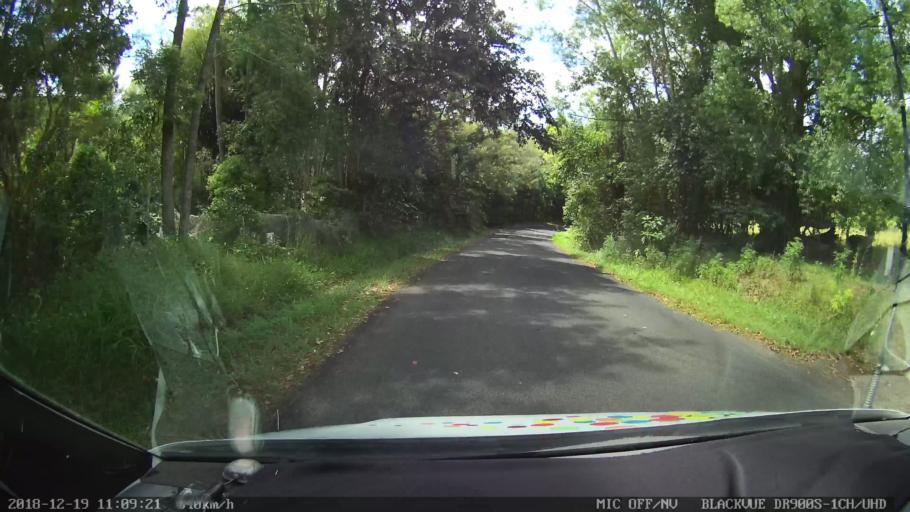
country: AU
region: New South Wales
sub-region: Lismore Municipality
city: Nimbin
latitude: -28.6341
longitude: 153.2644
